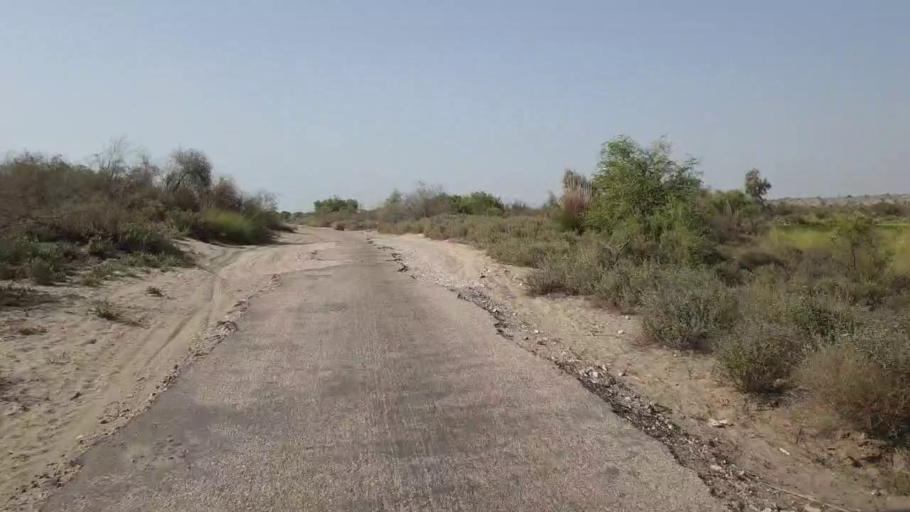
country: PK
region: Sindh
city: Jam Sahib
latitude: 26.5908
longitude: 68.9221
